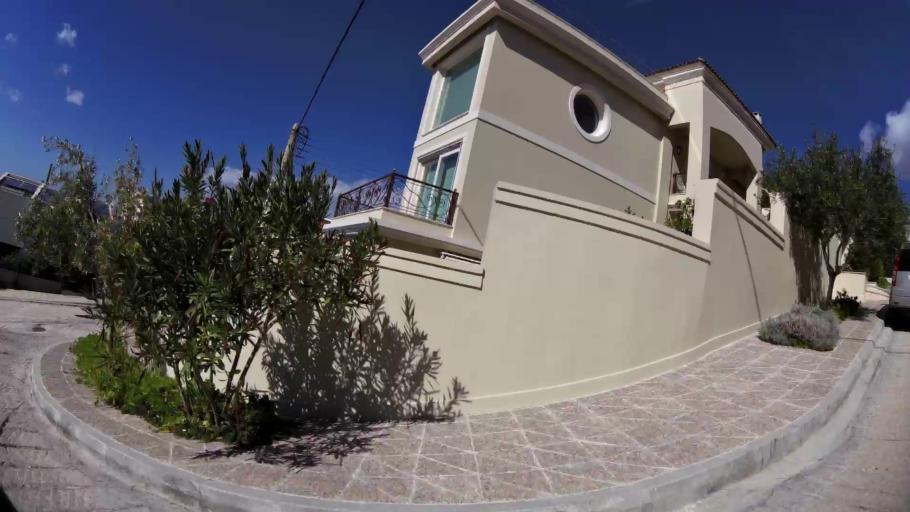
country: GR
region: Attica
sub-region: Nomarchia Anatolikis Attikis
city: Voula
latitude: 37.8580
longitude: 23.7828
